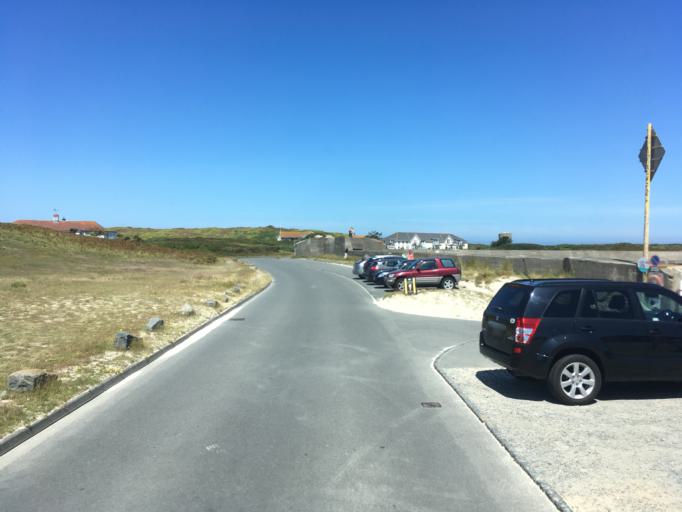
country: GG
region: St Peter Port
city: Saint Peter Port
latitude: 49.5036
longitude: -2.5334
